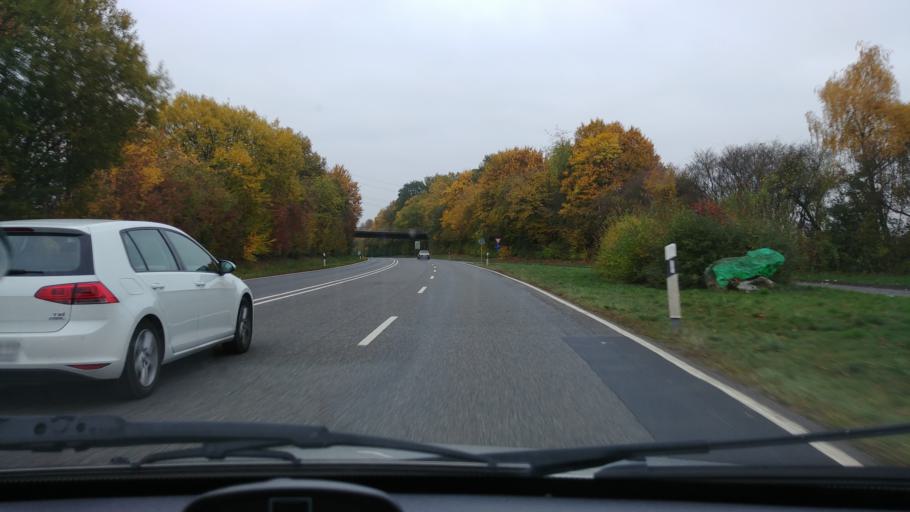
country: DE
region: Hesse
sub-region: Regierungsbezirk Giessen
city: Elz
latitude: 50.4608
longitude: 8.0632
